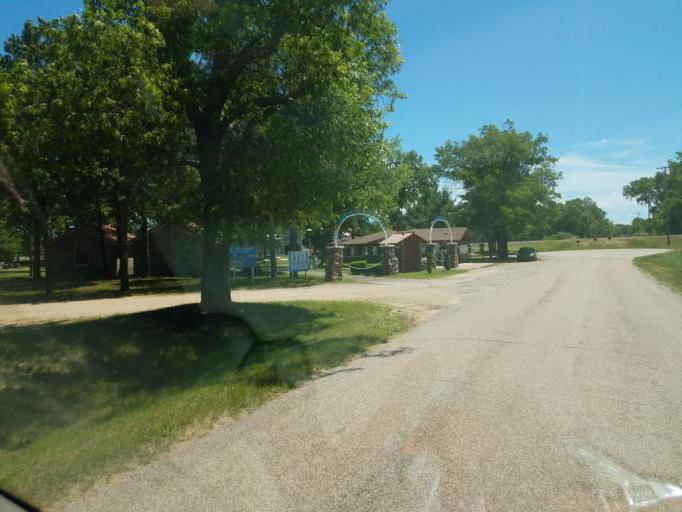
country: US
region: Wisconsin
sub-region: Juneau County
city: New Lisbon
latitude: 44.0213
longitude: -90.0576
